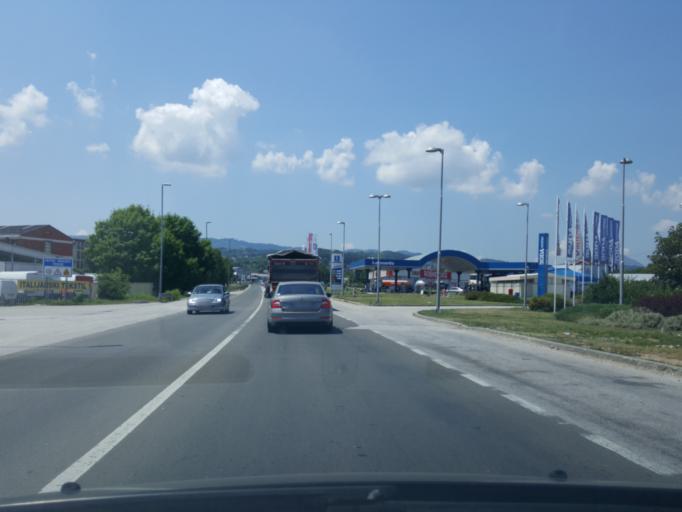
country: RS
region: Central Serbia
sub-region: Moravicki Okrug
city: Cacak
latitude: 43.8780
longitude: 20.3563
